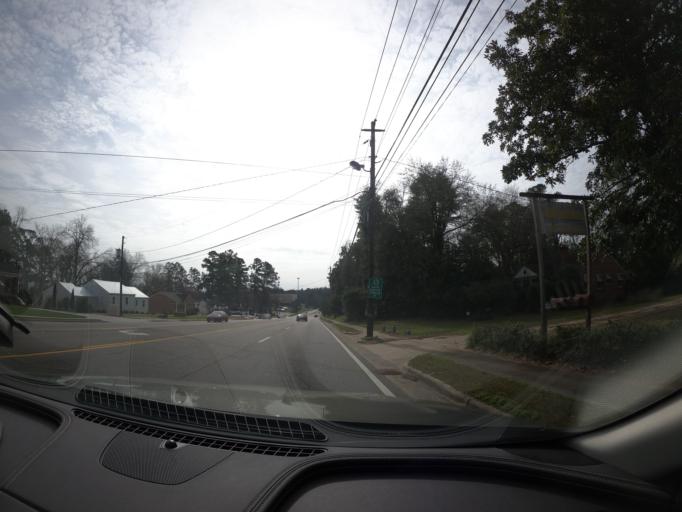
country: US
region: Georgia
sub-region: Richmond County
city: Augusta
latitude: 33.4953
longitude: -82.0107
